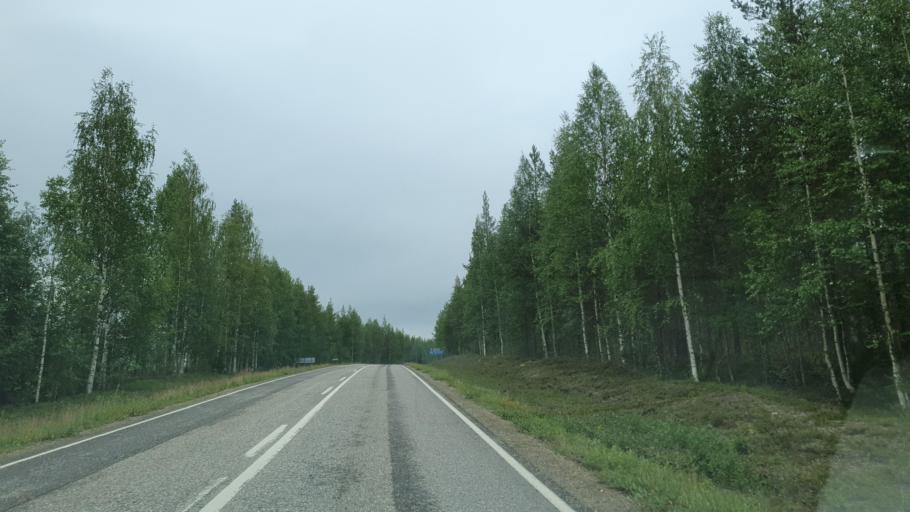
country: FI
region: Lapland
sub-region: Itae-Lappi
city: Pyhaejaervi
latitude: 67.3529
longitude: 26.9965
